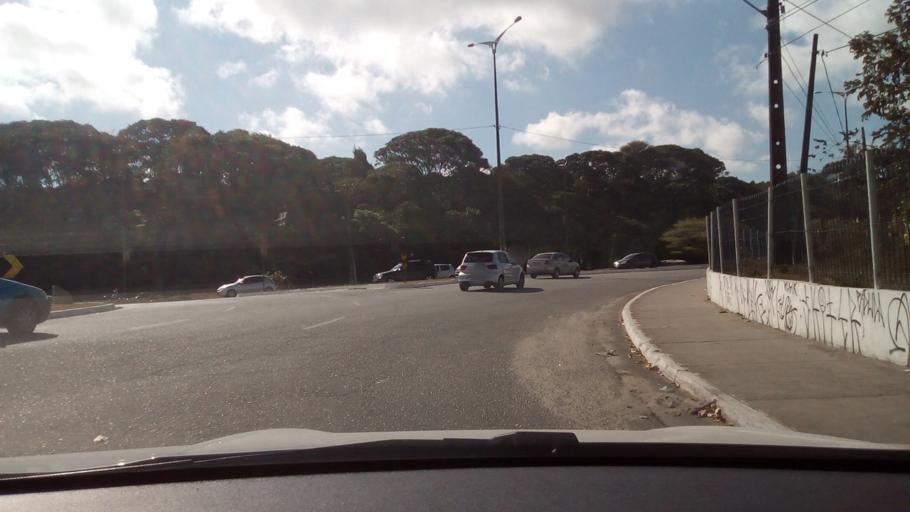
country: BR
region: Paraiba
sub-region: Joao Pessoa
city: Joao Pessoa
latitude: -7.1450
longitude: -34.8503
